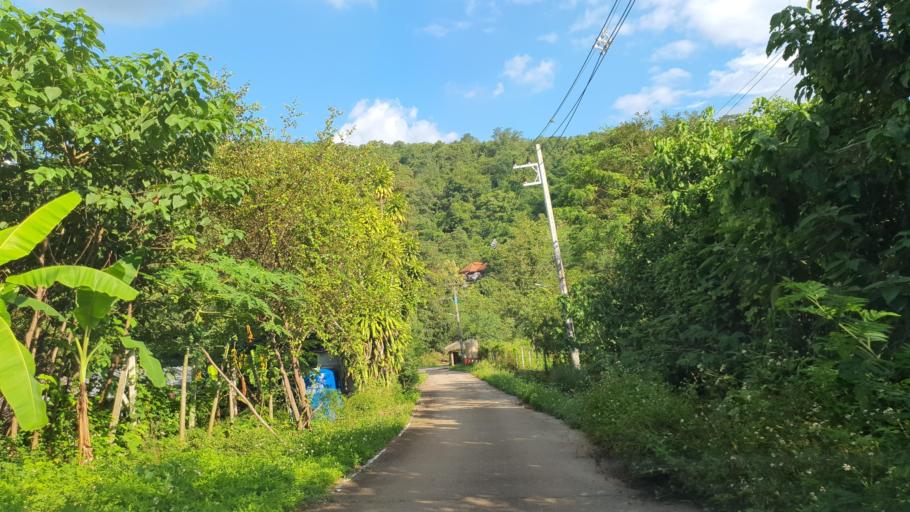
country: TH
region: Chiang Mai
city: Hang Dong
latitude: 18.7592
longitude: 98.8686
